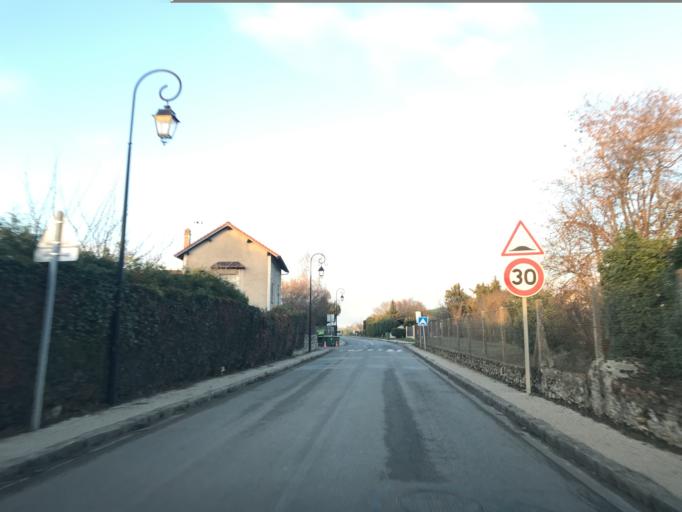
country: FR
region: Ile-de-France
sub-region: Departement des Yvelines
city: Galluis
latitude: 48.8209
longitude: 1.8190
